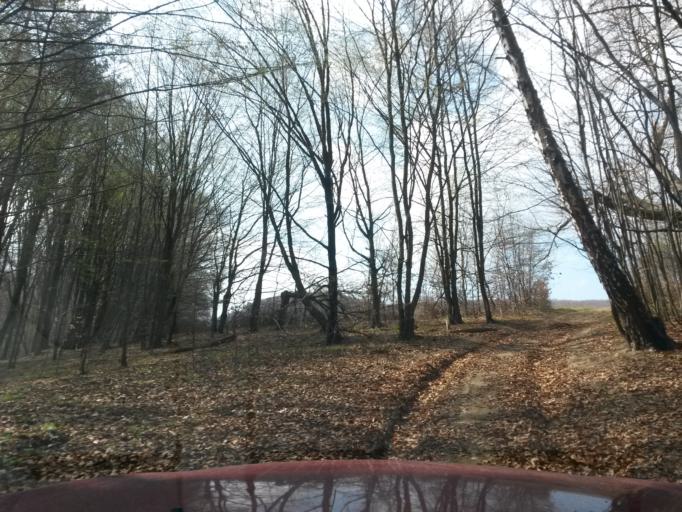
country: SK
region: Presovsky
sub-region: Okres Presov
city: Presov
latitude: 48.9352
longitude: 21.1466
